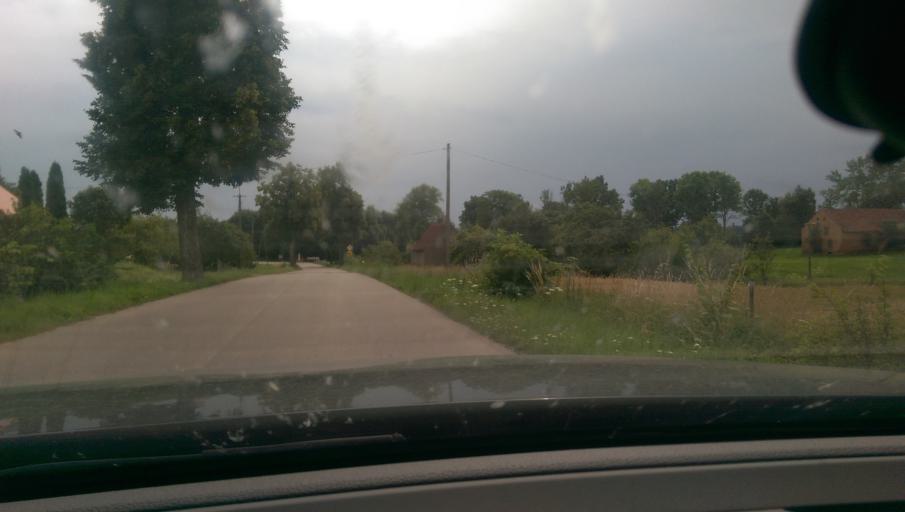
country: PL
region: Podlasie
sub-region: Powiat suwalski
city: Raczki
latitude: 53.9396
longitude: 22.6888
